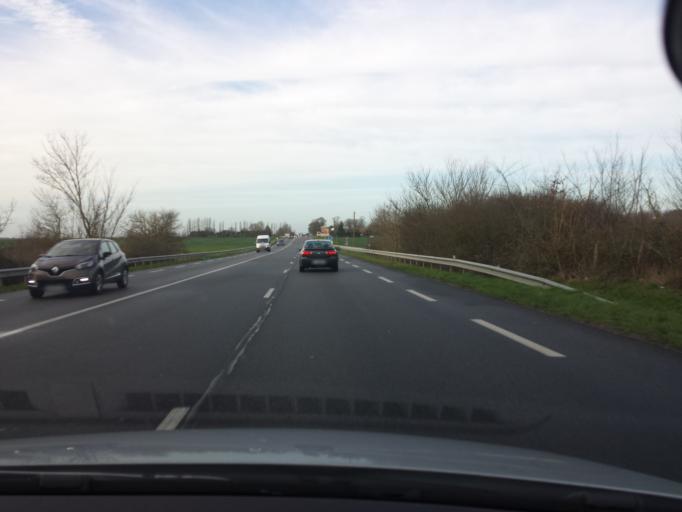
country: FR
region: Haute-Normandie
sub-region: Departement de l'Eure
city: Gravigny
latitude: 49.0137
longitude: 1.2536
